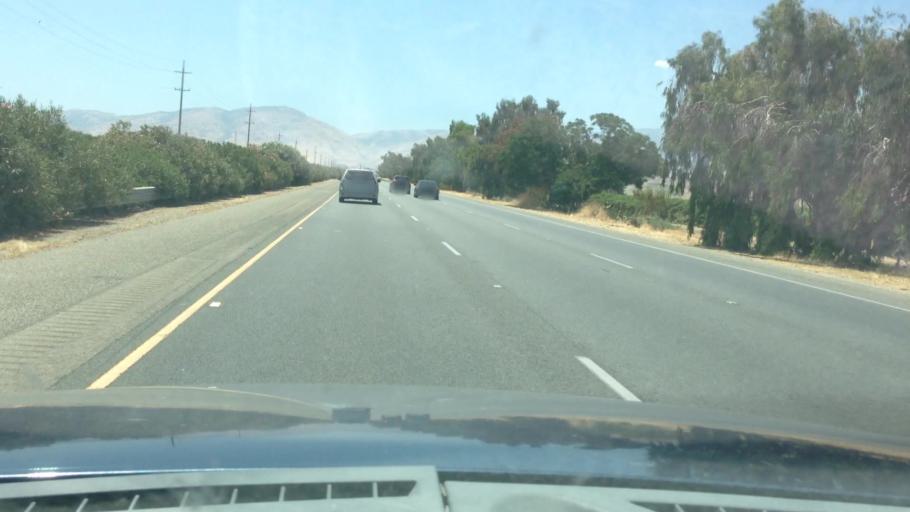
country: US
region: California
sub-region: Kern County
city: Weedpatch
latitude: 35.0457
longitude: -118.9640
